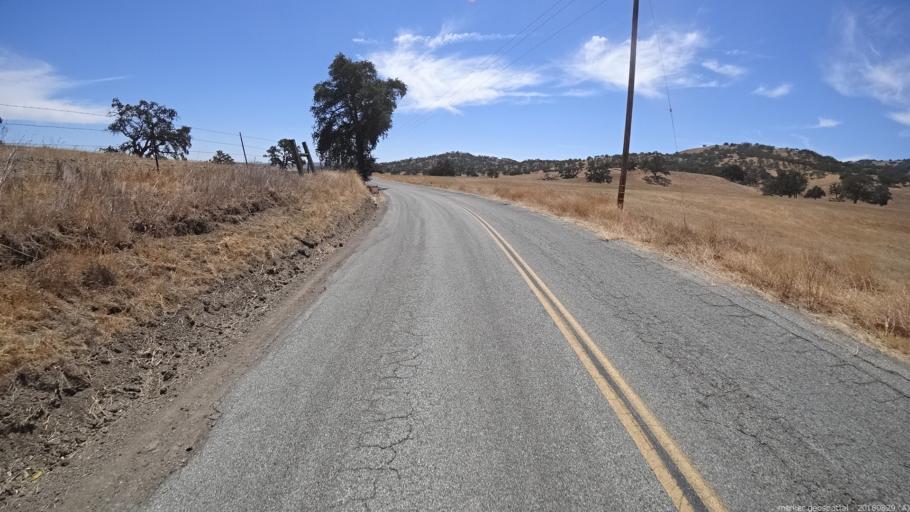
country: US
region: California
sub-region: San Luis Obispo County
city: Lake Nacimiento
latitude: 35.8341
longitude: -120.8457
